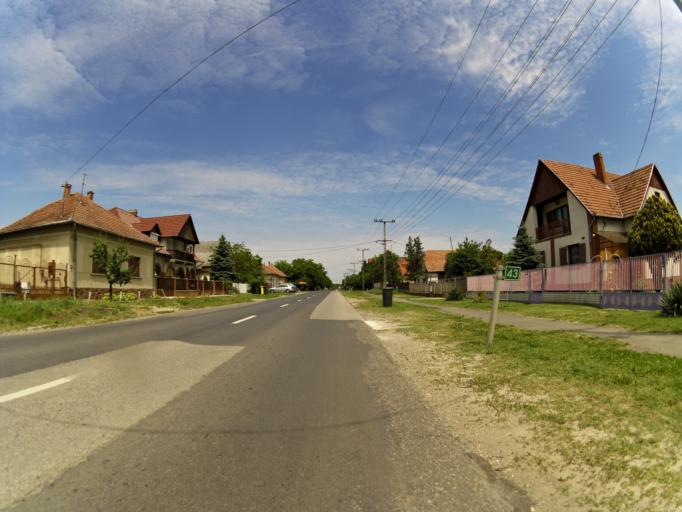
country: HU
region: Csongrad
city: Sandorfalva
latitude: 46.3714
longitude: 20.1147
